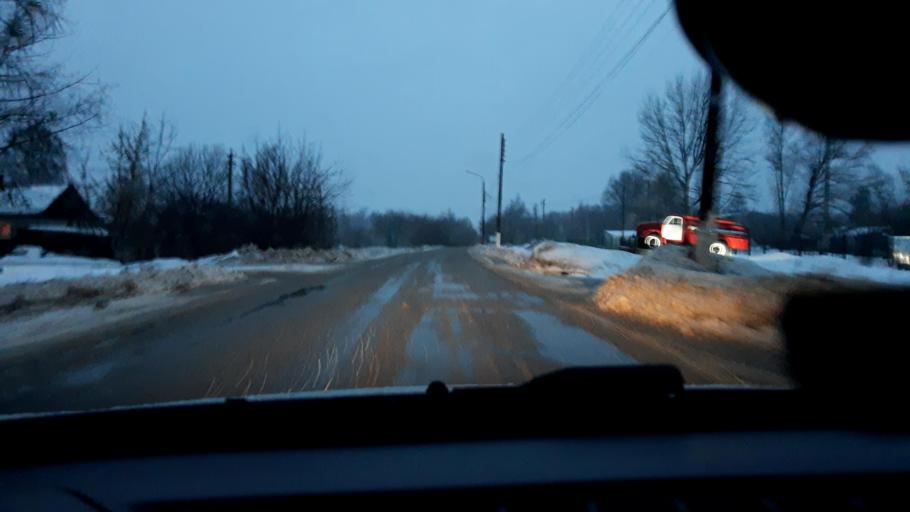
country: RU
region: Nizjnij Novgorod
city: Bogorodsk
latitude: 56.1072
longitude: 43.4890
